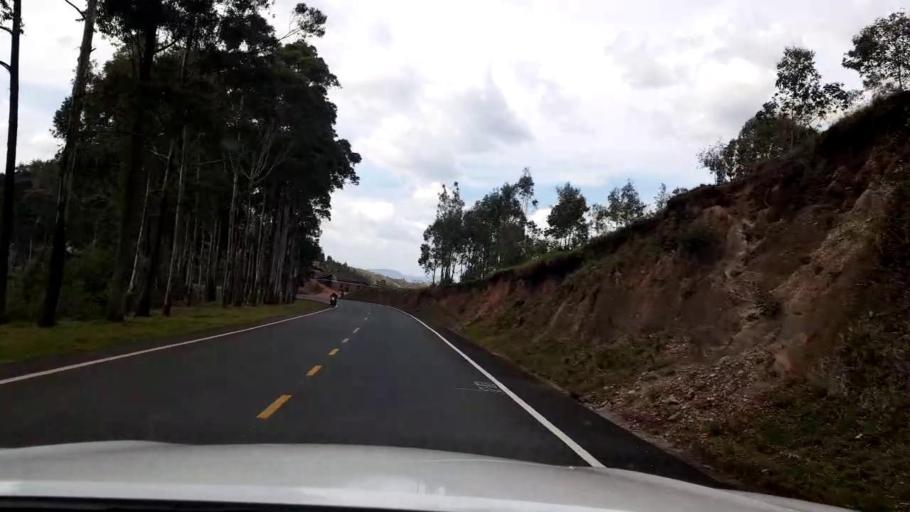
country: RW
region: Southern Province
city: Gitarama
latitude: -2.0268
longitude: 29.7175
